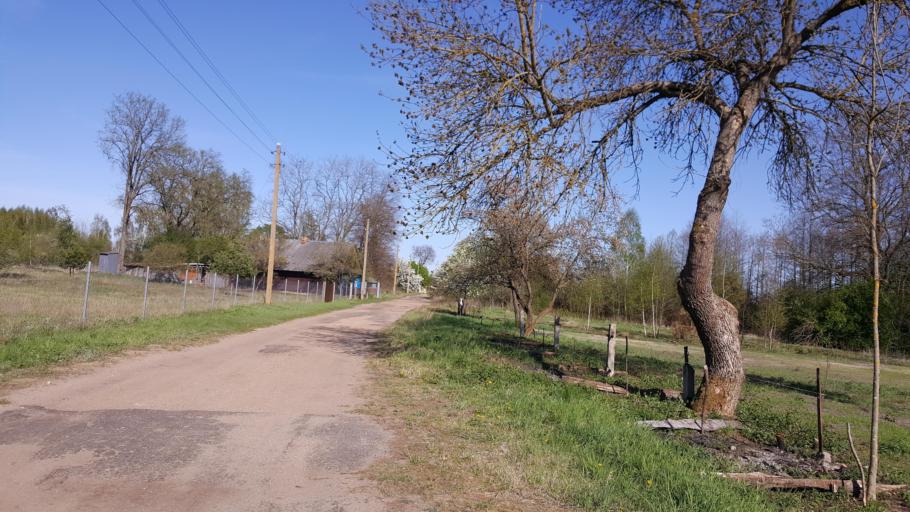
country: BY
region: Brest
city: Kamyanyets
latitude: 52.4409
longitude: 23.8867
